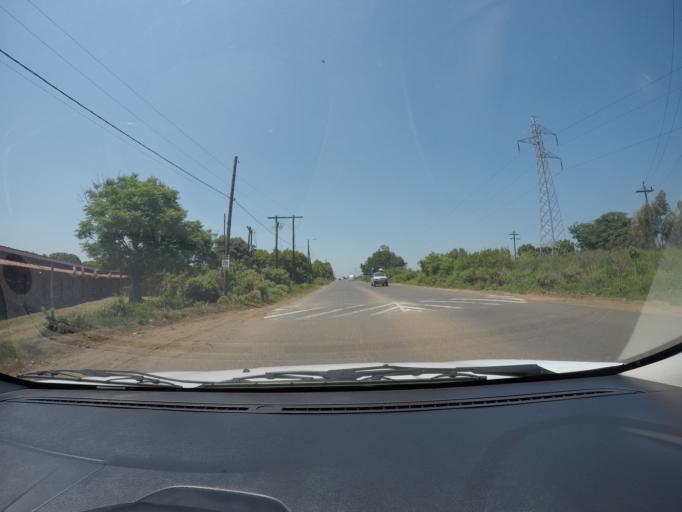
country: ZA
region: KwaZulu-Natal
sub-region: uThungulu District Municipality
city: eSikhawini
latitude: -28.8436
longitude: 31.9334
